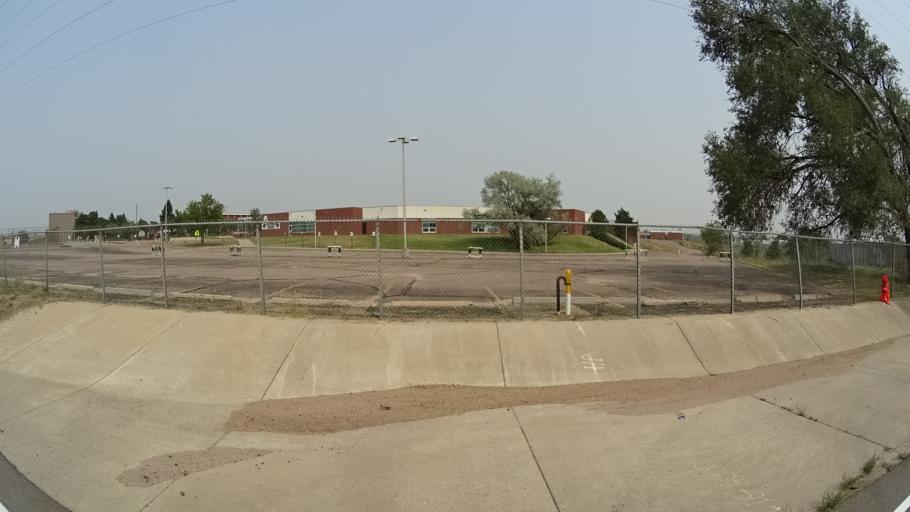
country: US
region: Colorado
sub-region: El Paso County
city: Stratmoor
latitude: 38.7918
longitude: -104.7947
